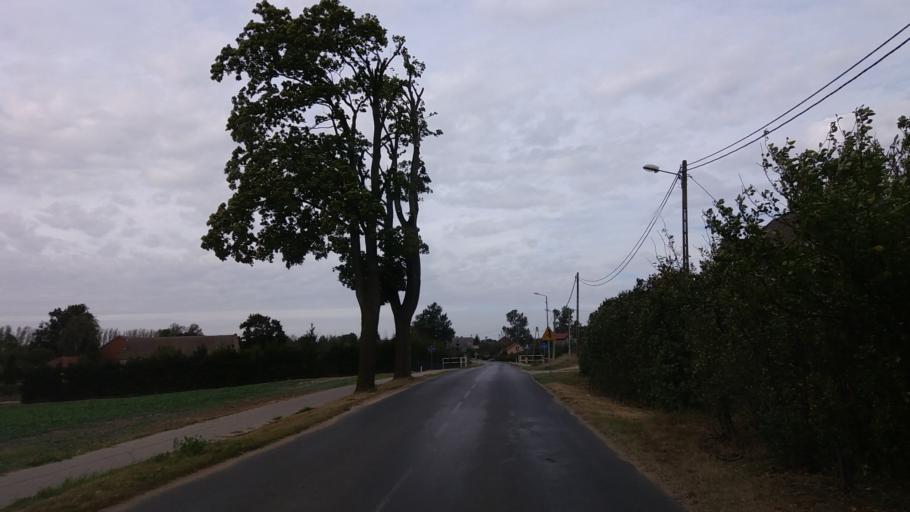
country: PL
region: Lubusz
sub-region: Powiat strzelecko-drezdenecki
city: Strzelce Krajenskie
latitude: 52.9005
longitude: 15.5053
